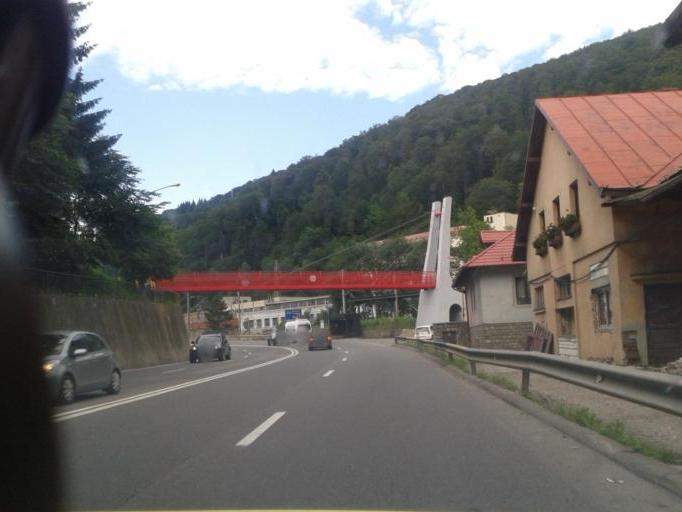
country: RO
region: Prahova
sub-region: Oras Sinaia
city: Sinaia
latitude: 45.3373
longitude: 25.5521
